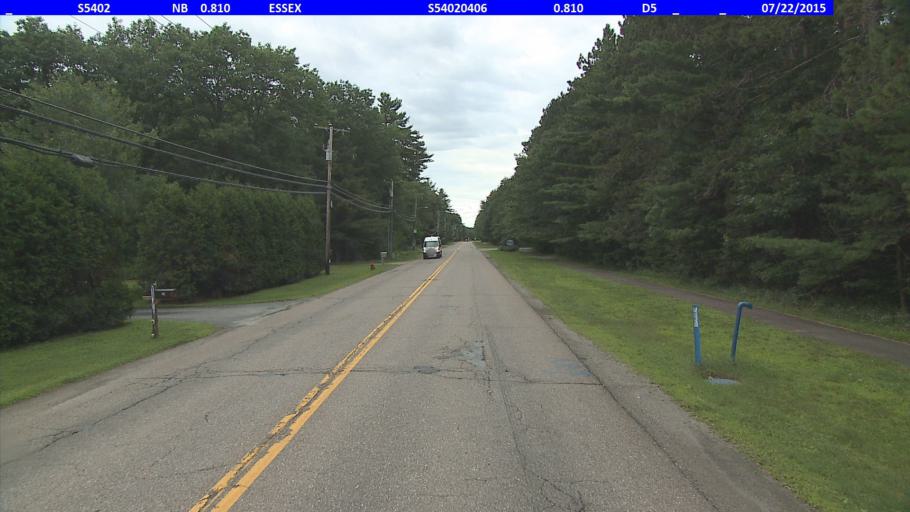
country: US
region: Vermont
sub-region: Chittenden County
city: Jericho
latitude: 44.4901
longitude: -73.0502
